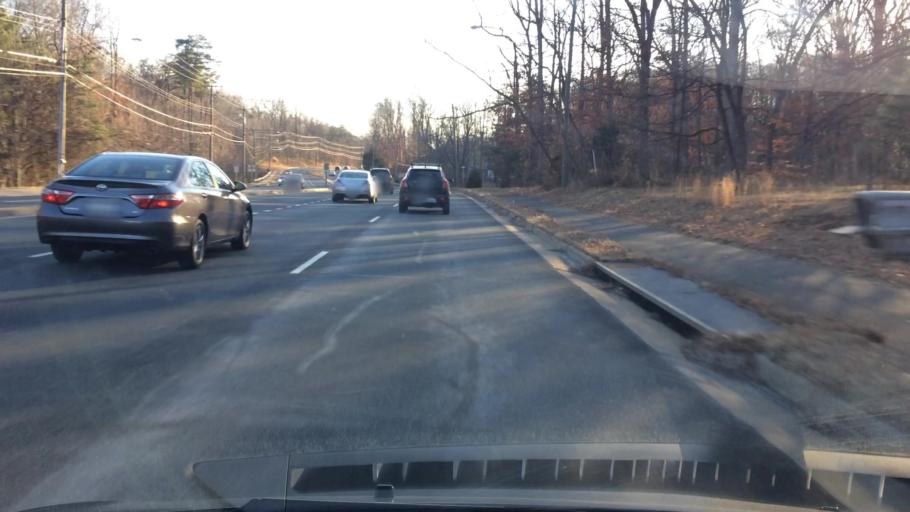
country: US
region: Virginia
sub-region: City of Fairfax
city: Fairfax
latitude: 38.8441
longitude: -77.3407
